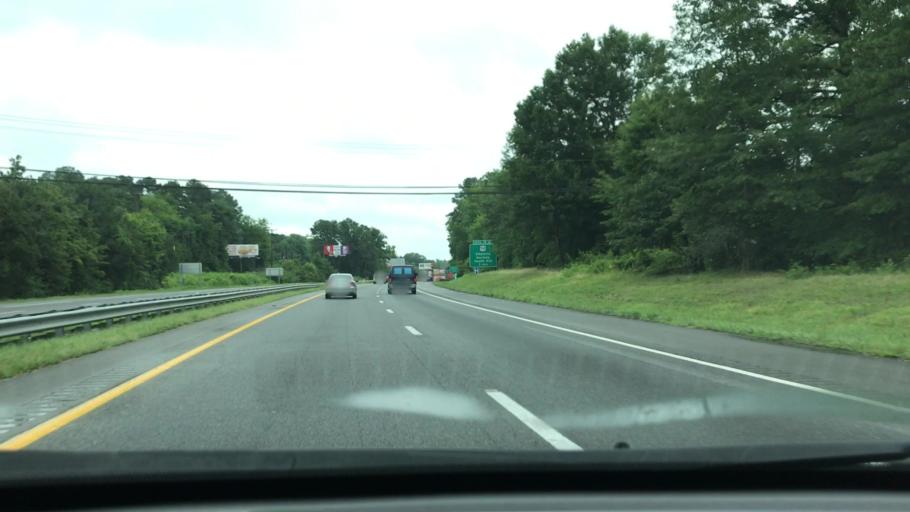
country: US
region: Virginia
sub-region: City of Emporia
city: Emporia
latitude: 36.6873
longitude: -77.5576
